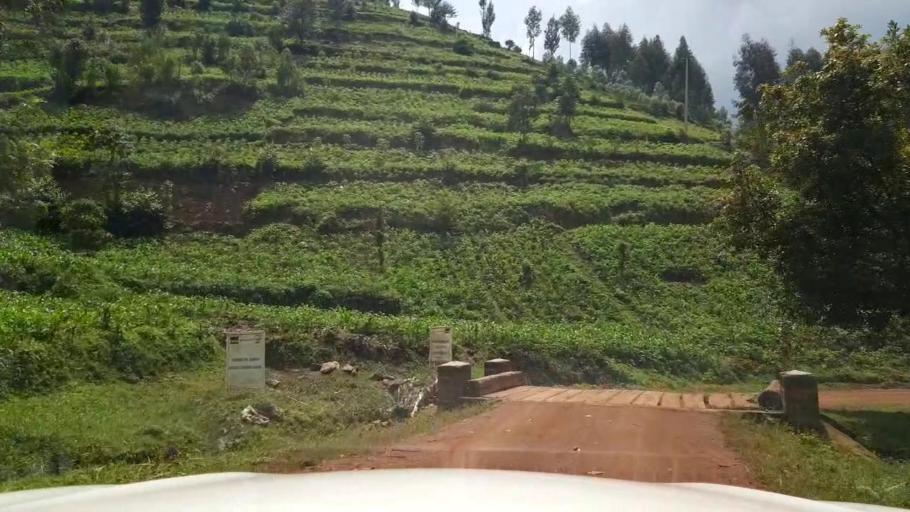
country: UG
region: Western Region
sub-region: Kisoro District
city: Kisoro
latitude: -1.3808
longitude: 29.7956
